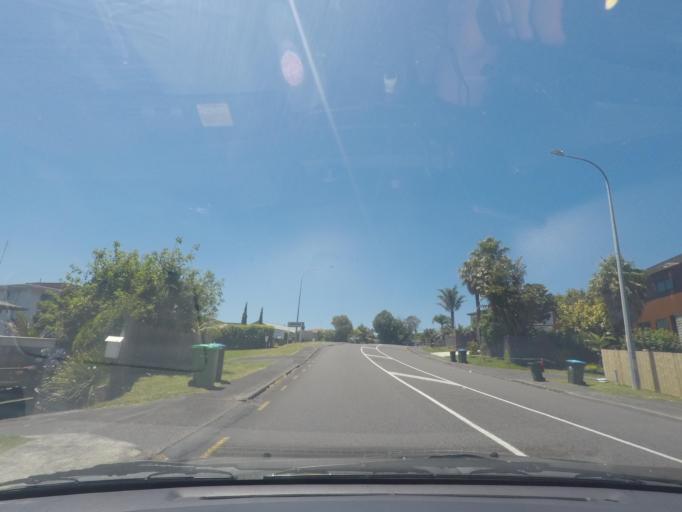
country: NZ
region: Auckland
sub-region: Auckland
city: Mangere
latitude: -36.9292
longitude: 174.7467
